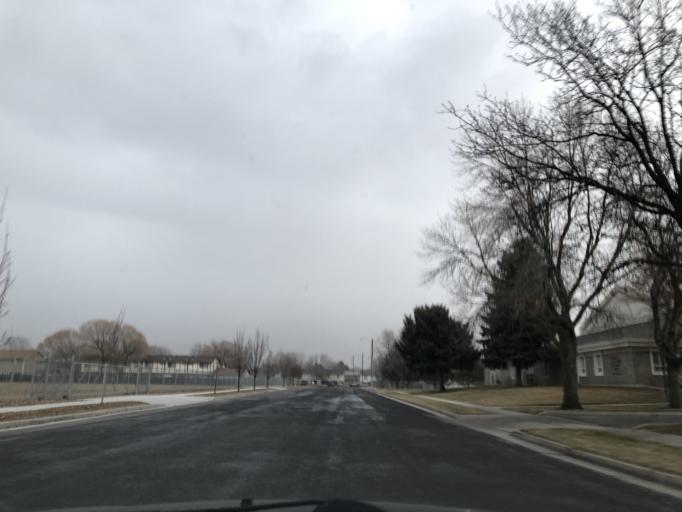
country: US
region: Utah
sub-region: Cache County
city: Logan
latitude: 41.7187
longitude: -111.8450
